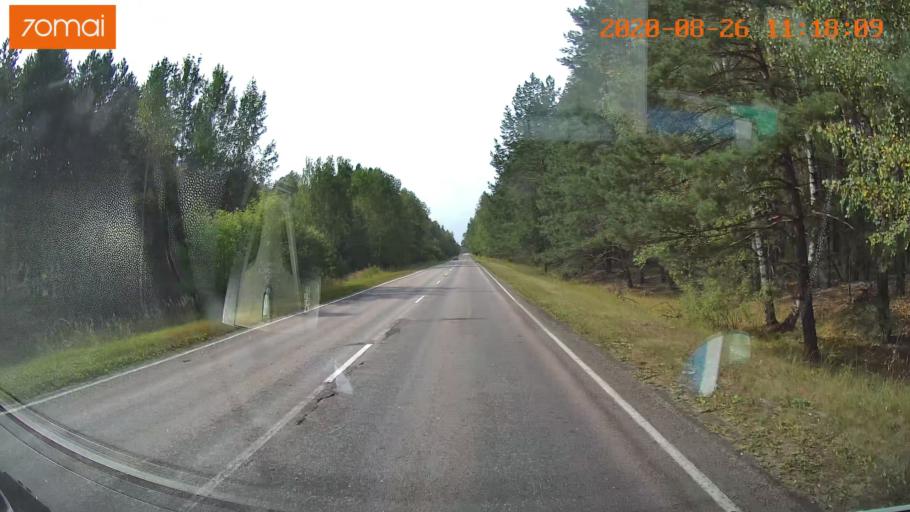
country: RU
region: Rjazan
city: Shilovo
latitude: 54.4128
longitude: 41.1021
